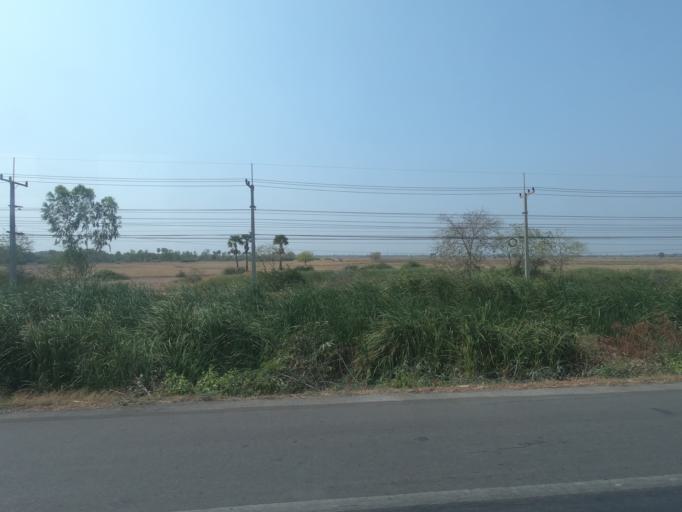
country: TH
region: Nakhon Ratchasima
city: Phimai
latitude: 15.3232
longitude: 102.4354
